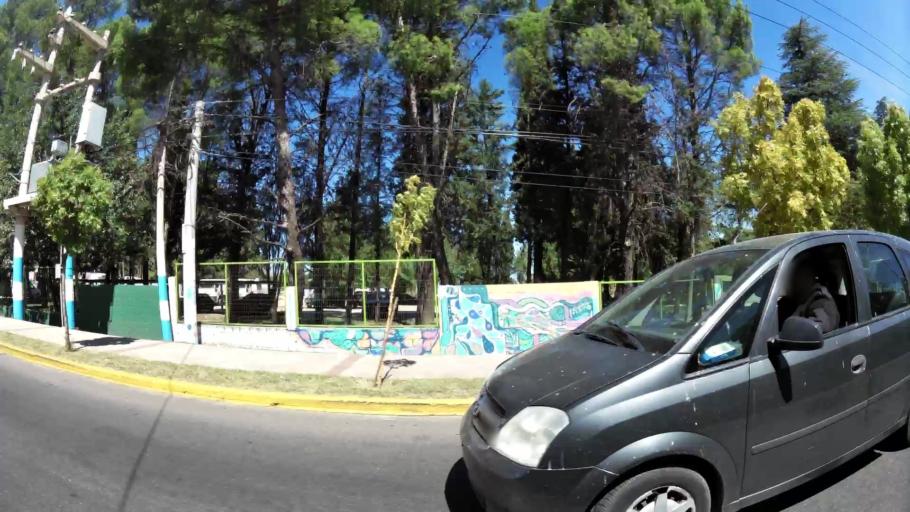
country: AR
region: San Luis
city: San Luis
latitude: -33.2943
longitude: -66.3060
